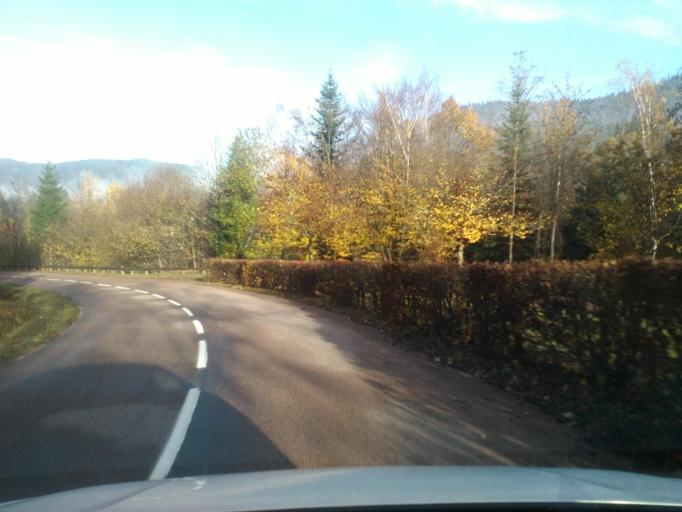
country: FR
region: Lorraine
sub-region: Departement des Vosges
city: Senones
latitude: 48.4173
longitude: 7.0495
